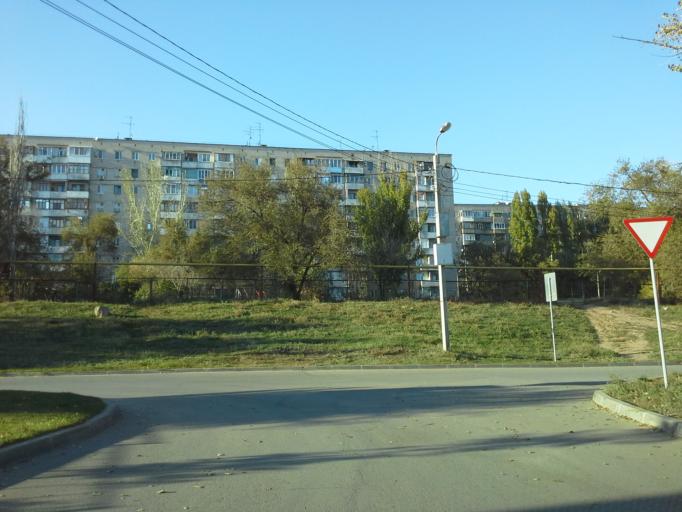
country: RU
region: Volgograd
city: Vodstroy
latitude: 48.8195
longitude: 44.6399
